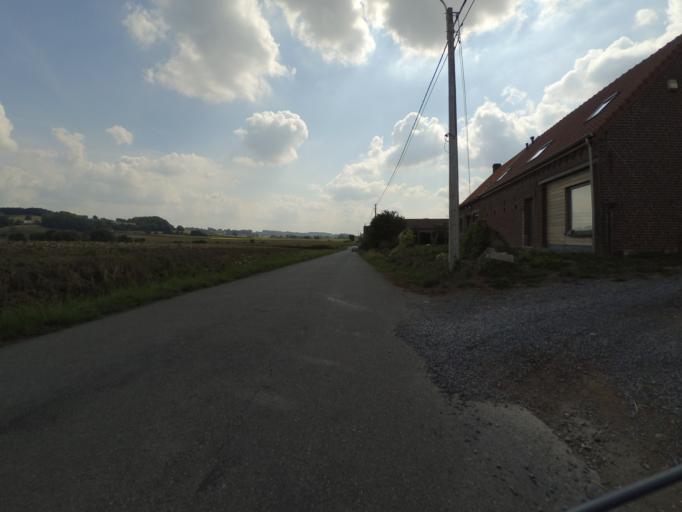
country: BE
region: Flanders
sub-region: Provincie Oost-Vlaanderen
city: Ronse
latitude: 50.7221
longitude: 3.6111
